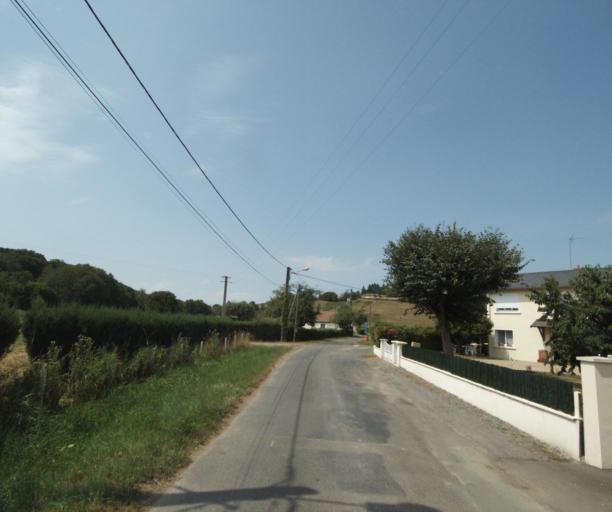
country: FR
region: Bourgogne
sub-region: Departement de Saone-et-Loire
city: Gueugnon
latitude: 46.6121
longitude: 4.0401
